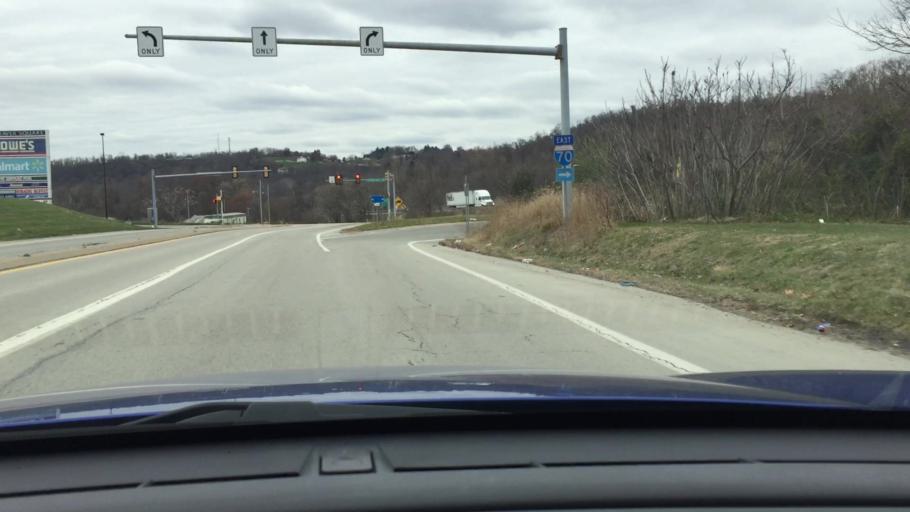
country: US
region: Pennsylvania
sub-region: Westmoreland County
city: Lynnwood-Pricedale
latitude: 40.1395
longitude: -79.8456
